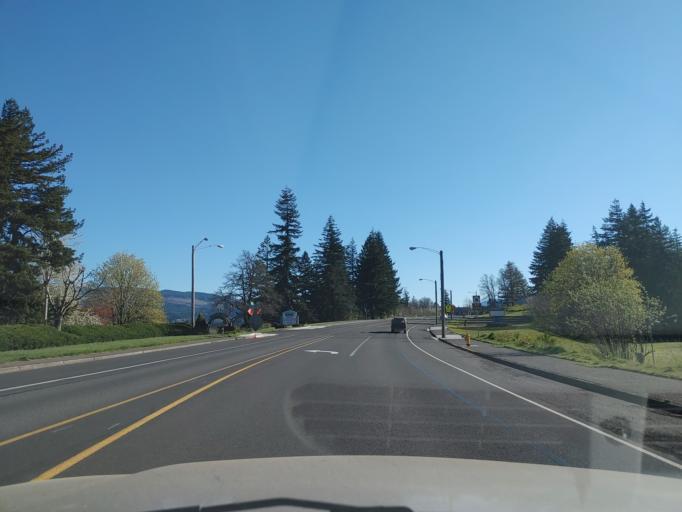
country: US
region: Oregon
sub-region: Hood River County
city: Cascade Locks
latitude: 45.6683
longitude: -121.8938
